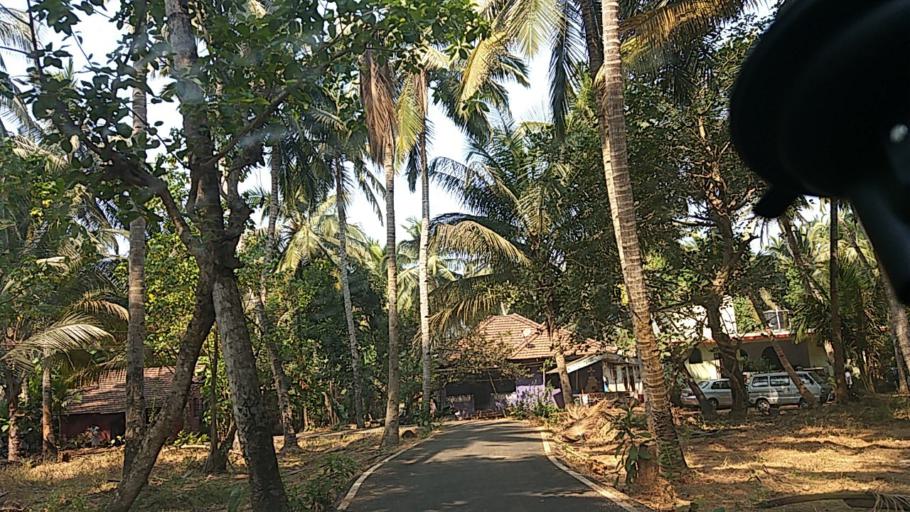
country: IN
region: Goa
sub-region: South Goa
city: Sancoale
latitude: 15.3387
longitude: 73.8969
